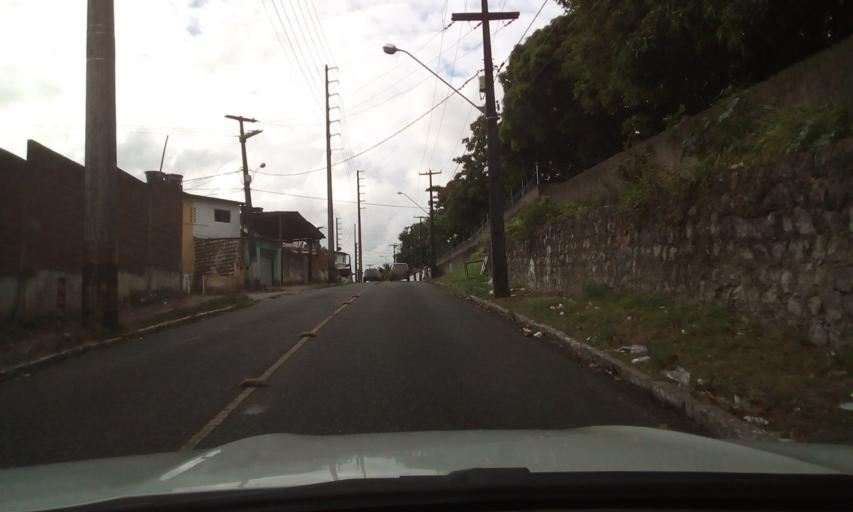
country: BR
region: Paraiba
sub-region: Joao Pessoa
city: Joao Pessoa
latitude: -7.1396
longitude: -34.8719
